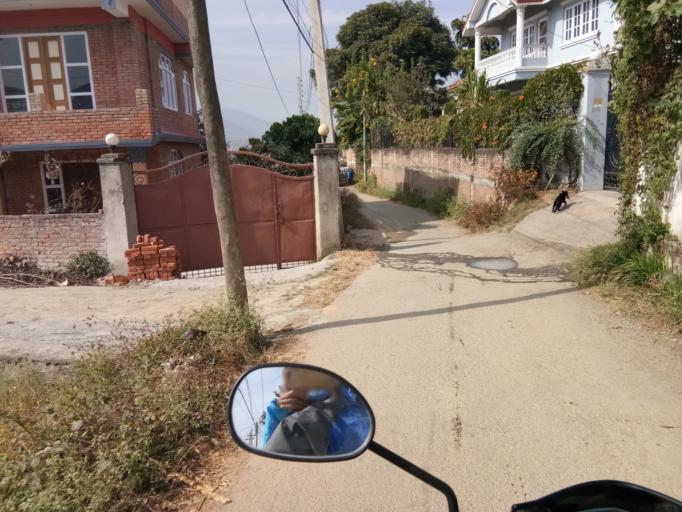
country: NP
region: Central Region
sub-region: Bagmati Zone
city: Patan
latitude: 27.6523
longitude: 85.2975
